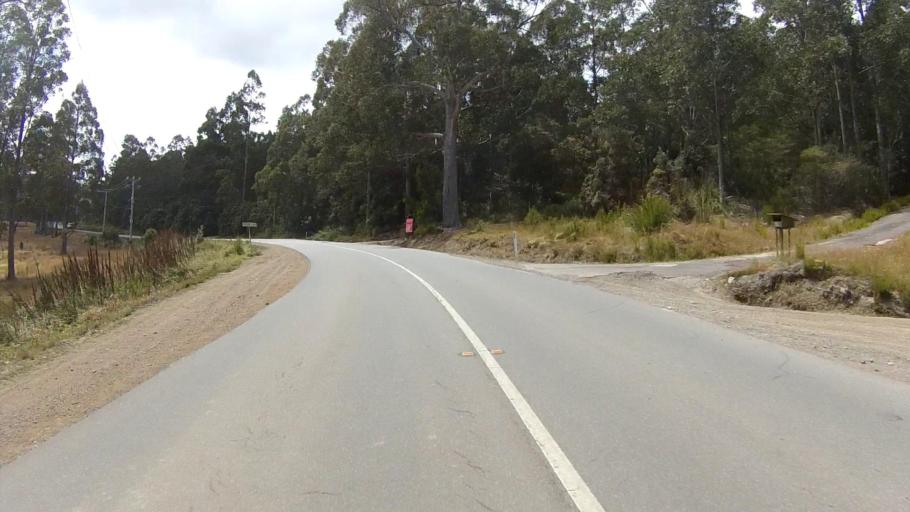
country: AU
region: Tasmania
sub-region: Kingborough
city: Kettering
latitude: -43.1237
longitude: 147.1841
